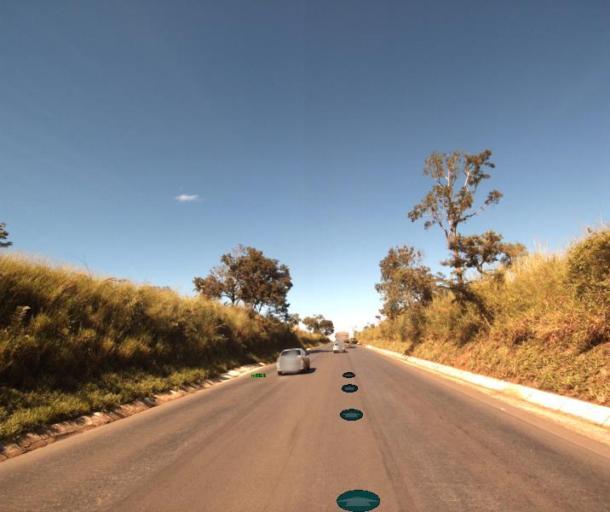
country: BR
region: Goias
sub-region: Itapaci
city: Itapaci
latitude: -15.0065
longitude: -49.4153
